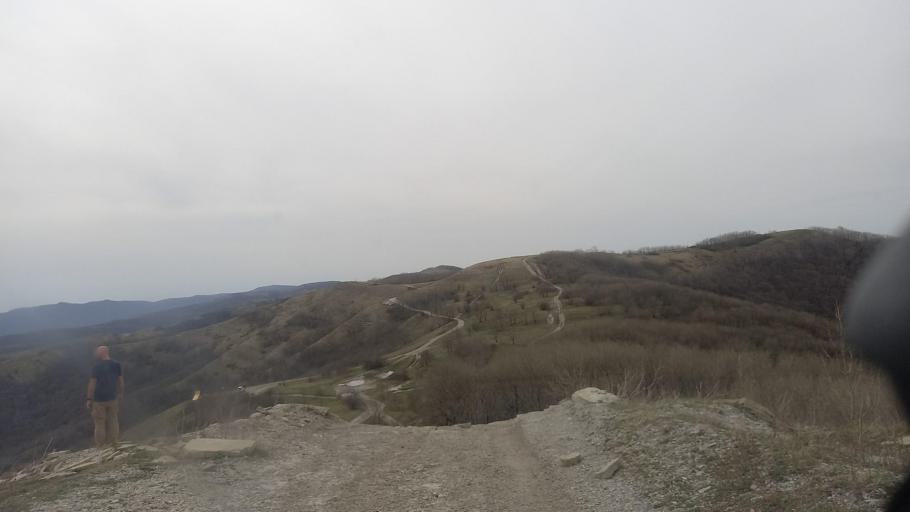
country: RU
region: Krasnodarskiy
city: Divnomorskoye
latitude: 44.6089
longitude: 38.2462
